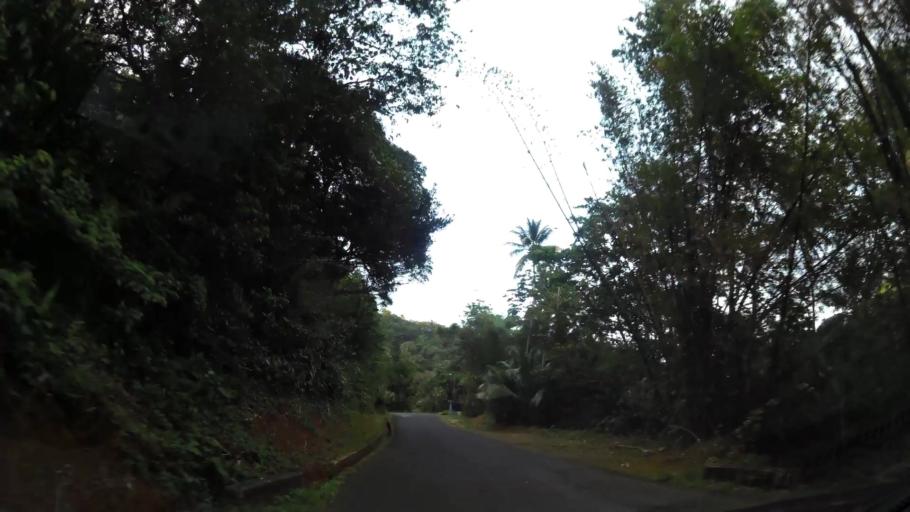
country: DM
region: Saint Andrew
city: Calibishie
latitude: 15.5890
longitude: -61.3945
